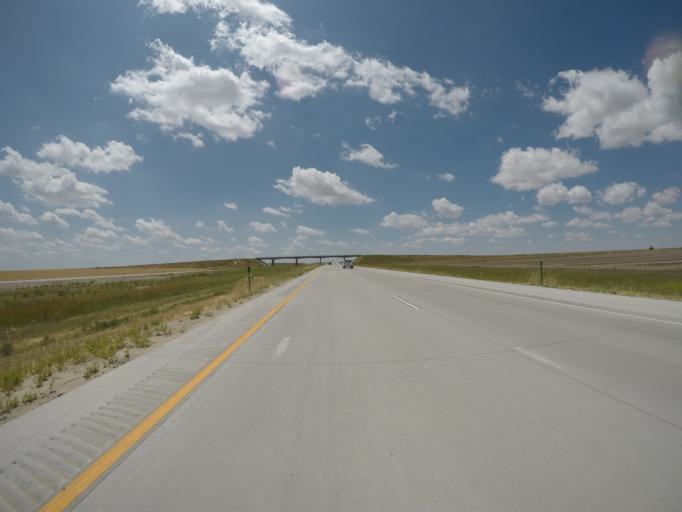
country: US
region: Colorado
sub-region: Kit Carson County
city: Burlington
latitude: 39.2943
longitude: -102.7781
